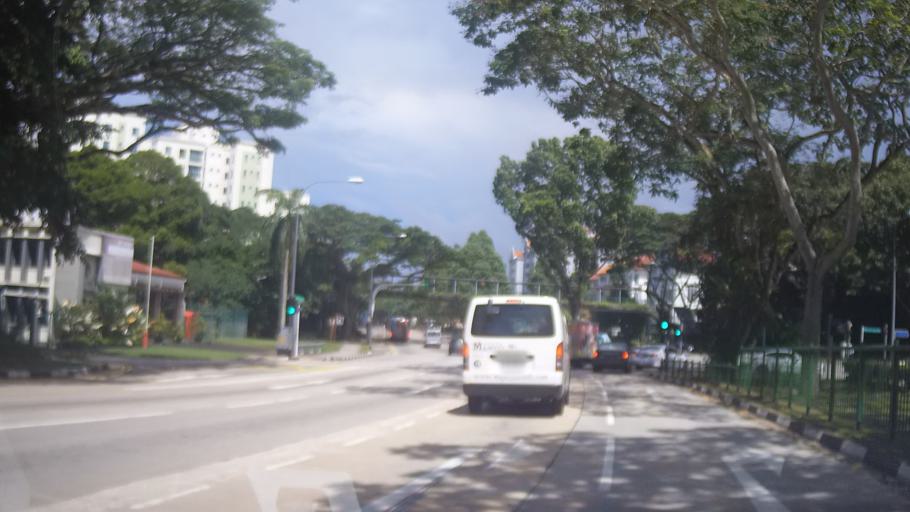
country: SG
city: Singapore
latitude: 1.3495
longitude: 103.7702
